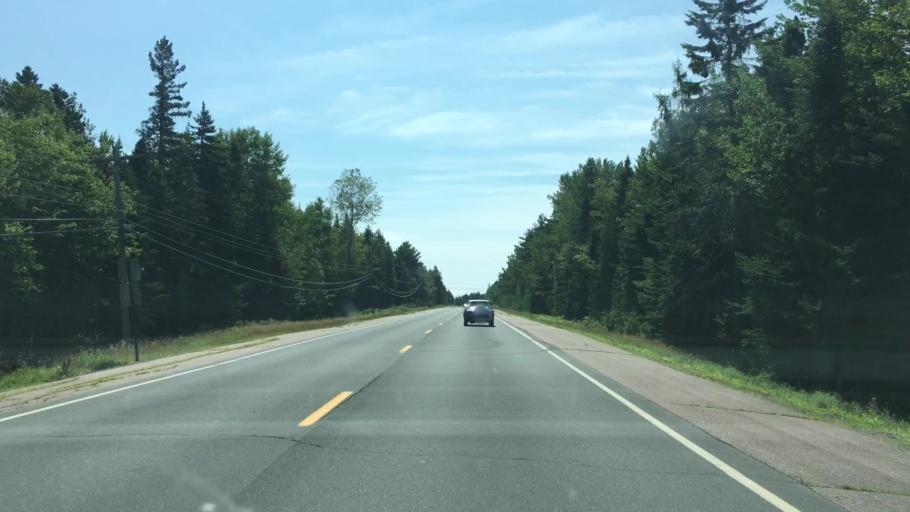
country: US
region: Maine
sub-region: Washington County
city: Calais
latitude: 45.1458
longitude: -67.1675
